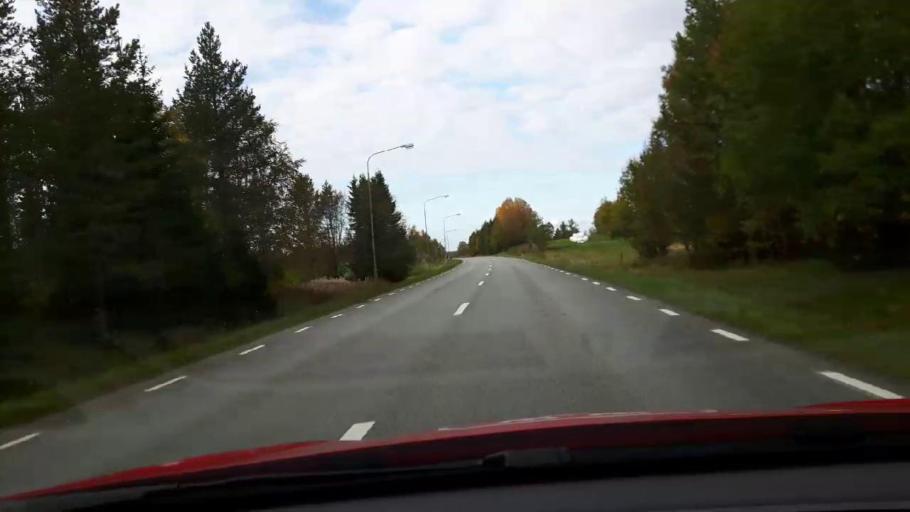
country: SE
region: Jaemtland
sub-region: Krokoms Kommun
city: Valla
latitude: 63.2358
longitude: 14.0080
